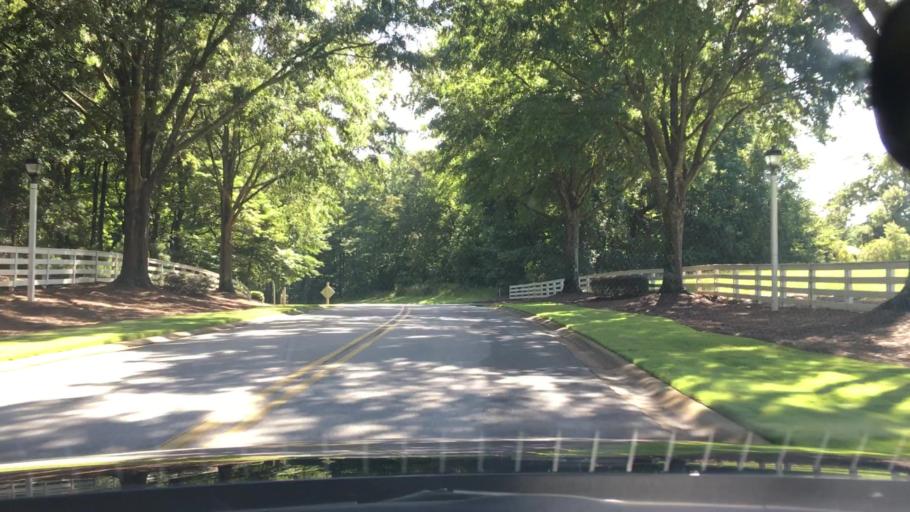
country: US
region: Georgia
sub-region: Putnam County
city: Jefferson
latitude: 33.3847
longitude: -83.2535
